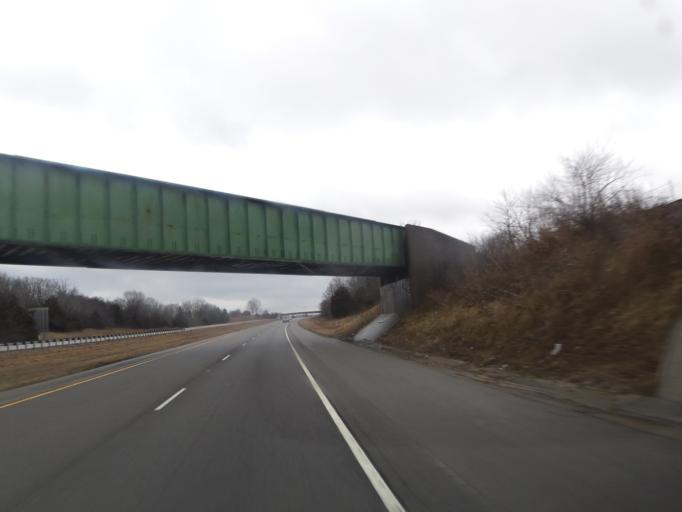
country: US
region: Illinois
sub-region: Johnson County
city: Goreville
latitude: 37.5839
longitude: -88.9695
